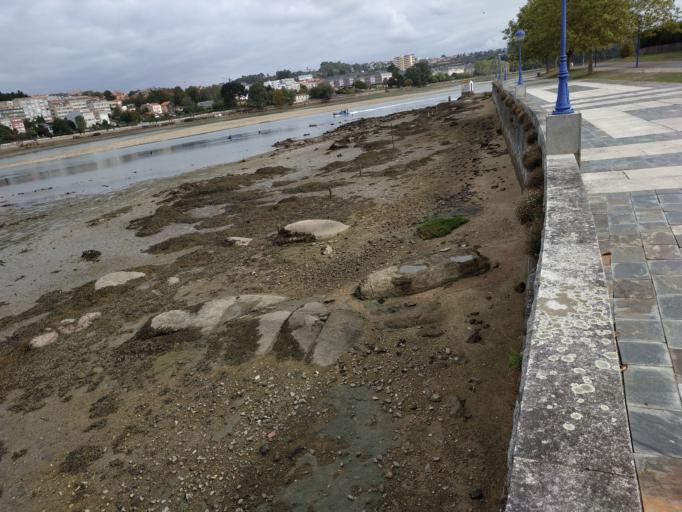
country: ES
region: Galicia
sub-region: Provincia da Coruna
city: Culleredo
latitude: 43.3295
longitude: -8.3812
